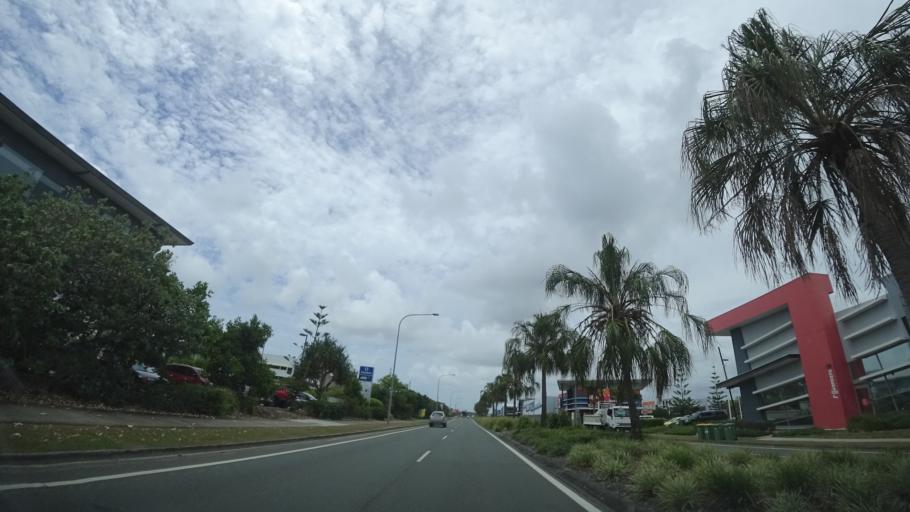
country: AU
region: Queensland
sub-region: Sunshine Coast
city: Mooloolaba
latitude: -26.7327
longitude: 153.1205
